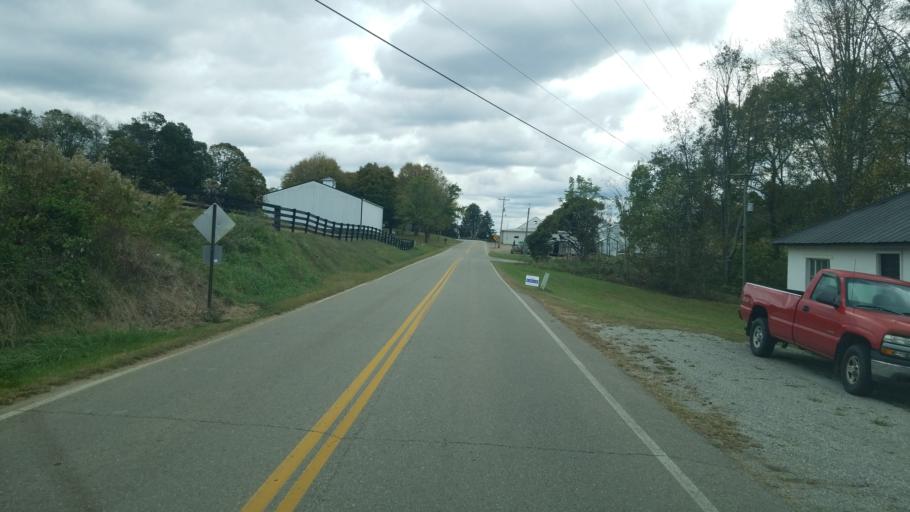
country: US
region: Ohio
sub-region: Jackson County
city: Jackson
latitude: 39.1475
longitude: -82.6678
